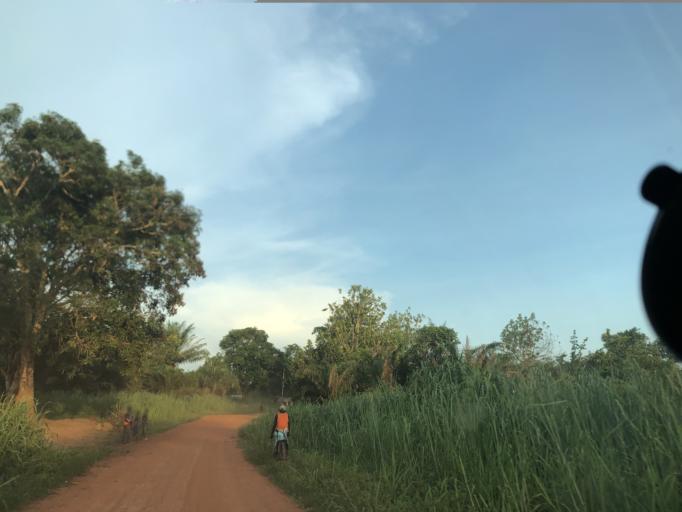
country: CF
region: Bangui
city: Bangui
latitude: 4.1643
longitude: 18.7734
